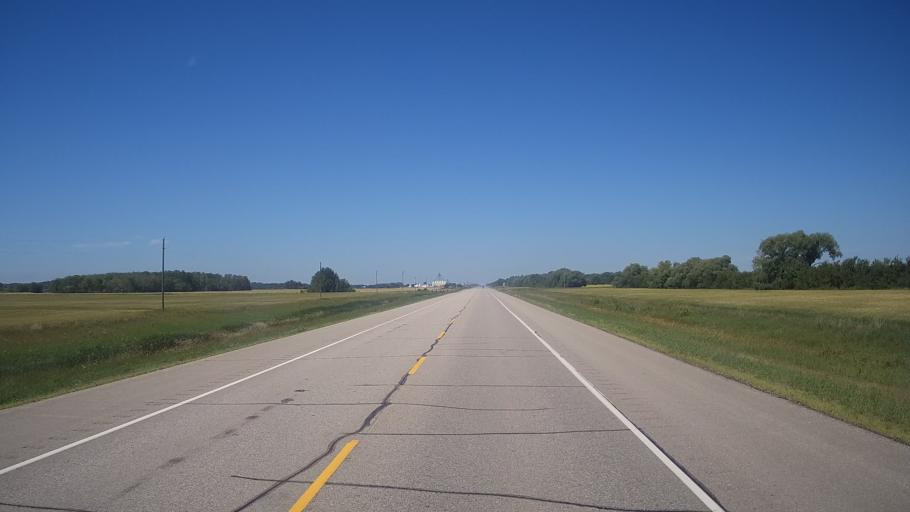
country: CA
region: Manitoba
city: Neepawa
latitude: 50.2257
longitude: -99.0137
